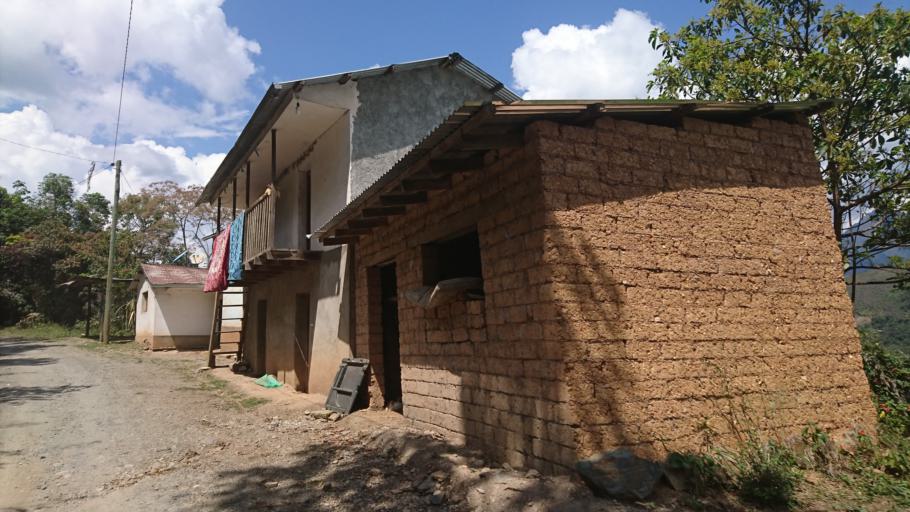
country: BO
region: La Paz
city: Coroico
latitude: -16.0773
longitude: -67.7845
